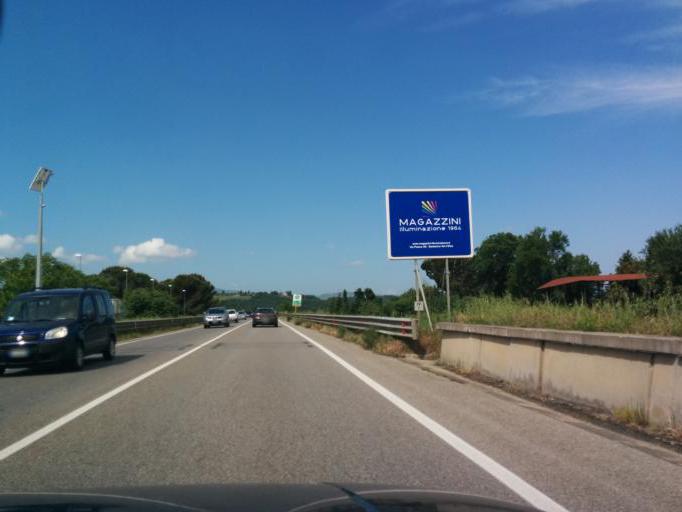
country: IT
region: Tuscany
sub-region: Provincia di Siena
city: Poggibonsi
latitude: 43.4826
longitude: 11.1339
